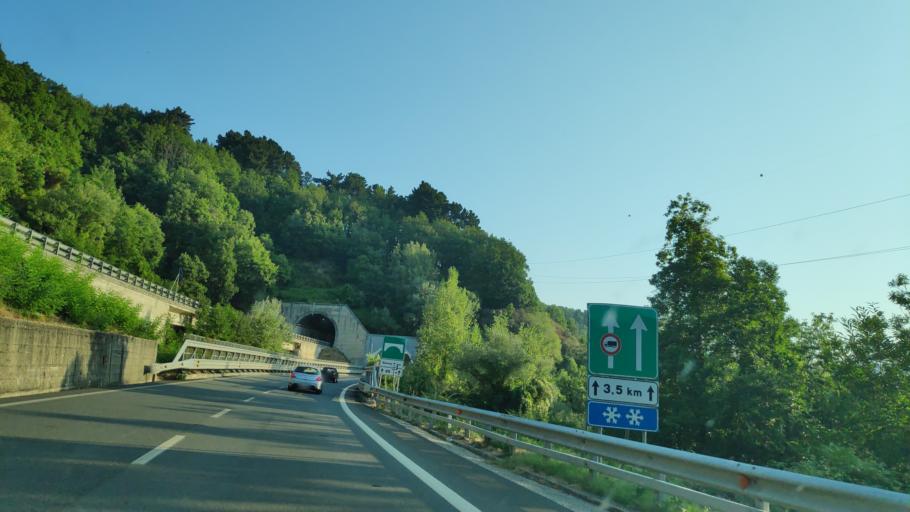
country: IT
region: Calabria
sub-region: Provincia di Cosenza
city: Belsito
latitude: 39.1741
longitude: 16.2939
